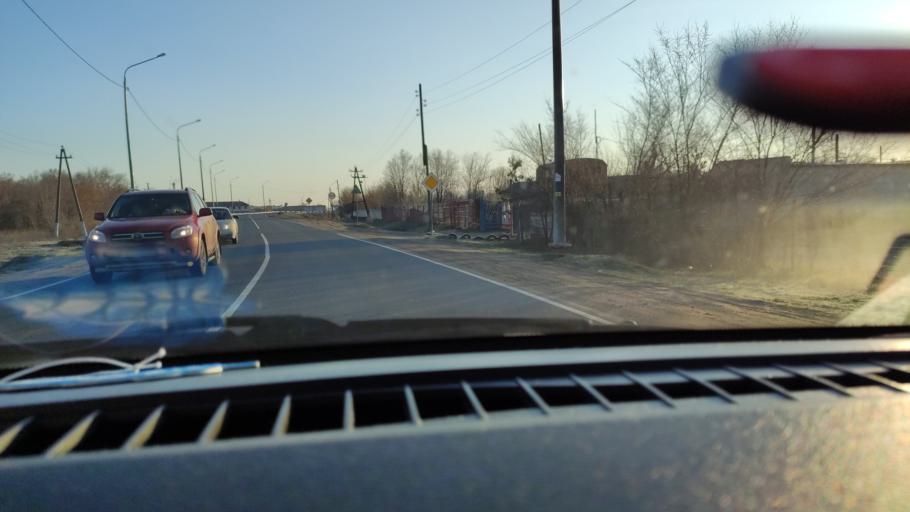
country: RU
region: Saratov
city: Sennoy
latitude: 52.1515
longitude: 46.9505
